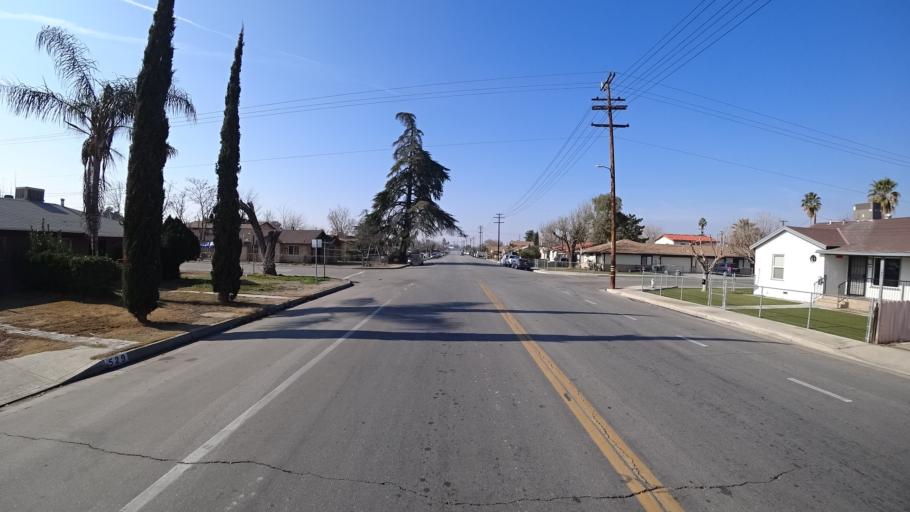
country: US
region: California
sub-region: Kern County
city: Bakersfield
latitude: 35.3864
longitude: -119.0084
